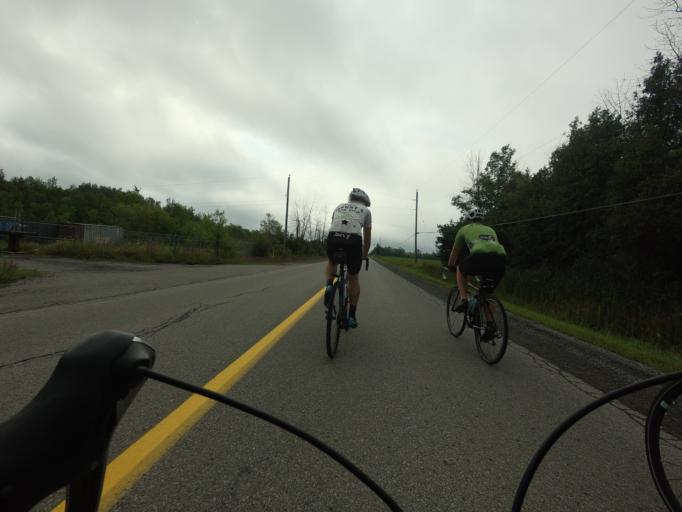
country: CA
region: Ontario
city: Bells Corners
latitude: 45.0997
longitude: -75.7666
